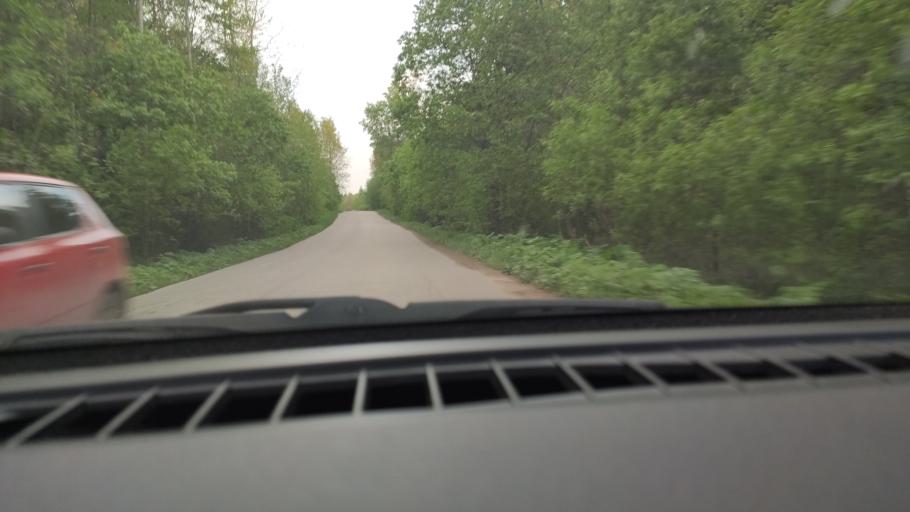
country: RU
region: Perm
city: Overyata
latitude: 58.0755
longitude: 56.0017
